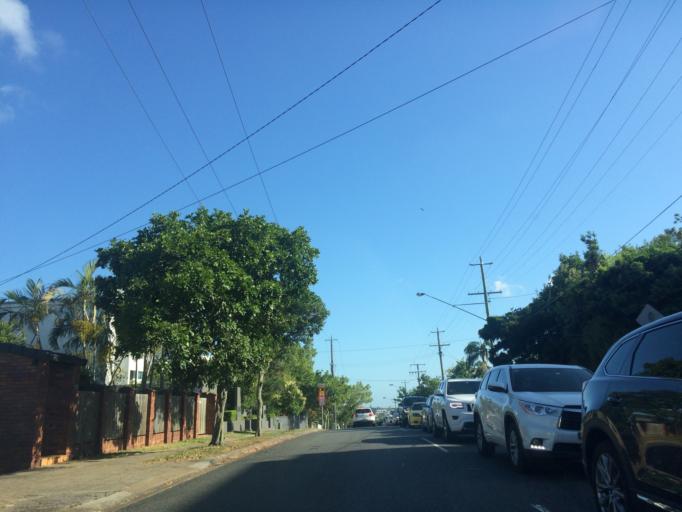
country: AU
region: Queensland
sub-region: Brisbane
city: Balmoral
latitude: -27.4714
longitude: 153.0589
